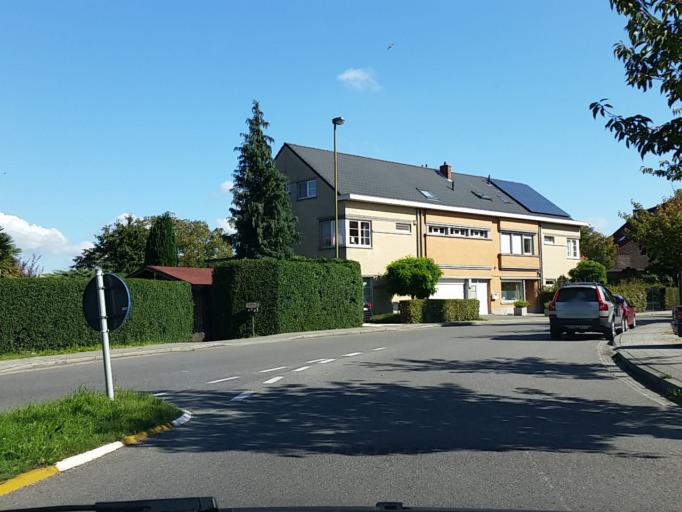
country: BE
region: Flanders
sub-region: Provincie Vlaams-Brabant
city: Leuven
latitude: 50.8905
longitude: 4.6916
